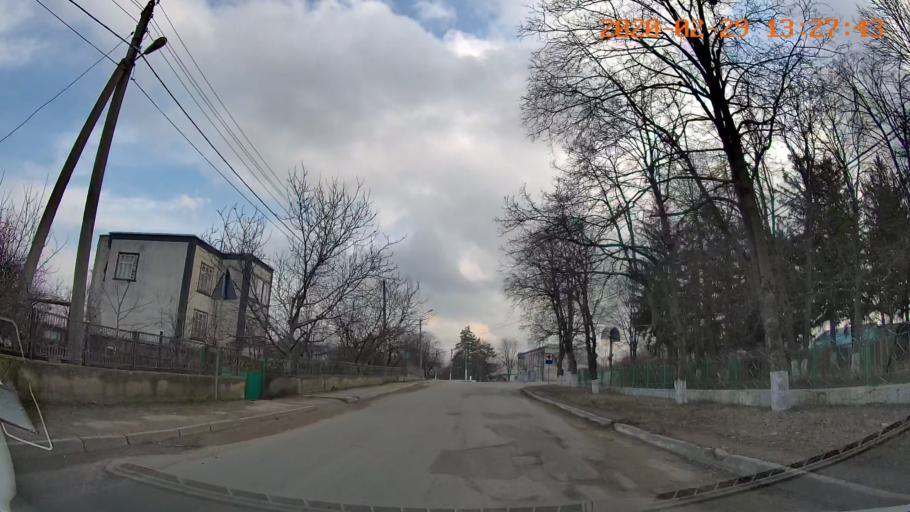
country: MD
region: Telenesti
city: Camenca
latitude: 47.9106
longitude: 28.6444
